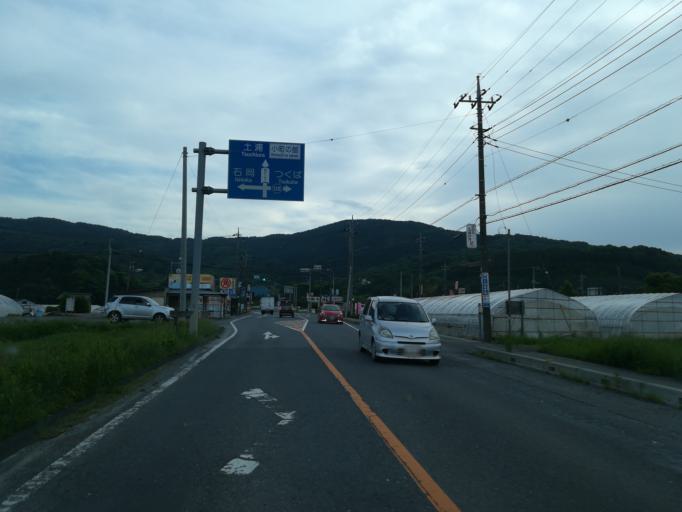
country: JP
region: Ibaraki
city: Tsukuba
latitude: 36.1888
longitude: 140.1710
